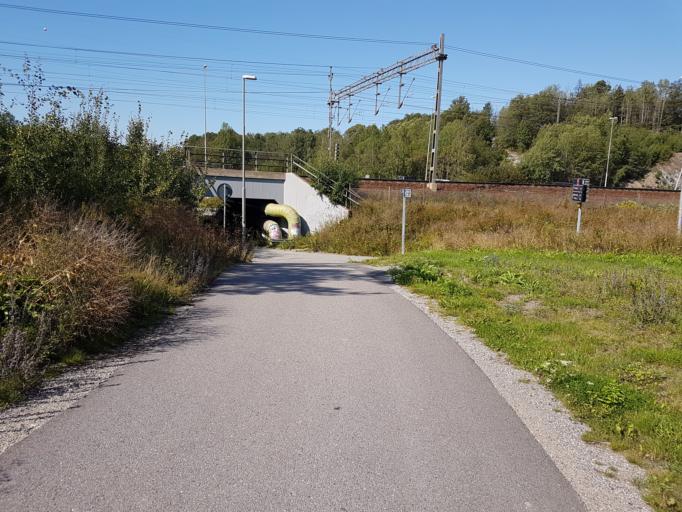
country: SE
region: Stockholm
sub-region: Huddinge Kommun
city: Huddinge
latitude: 59.2237
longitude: 17.9550
